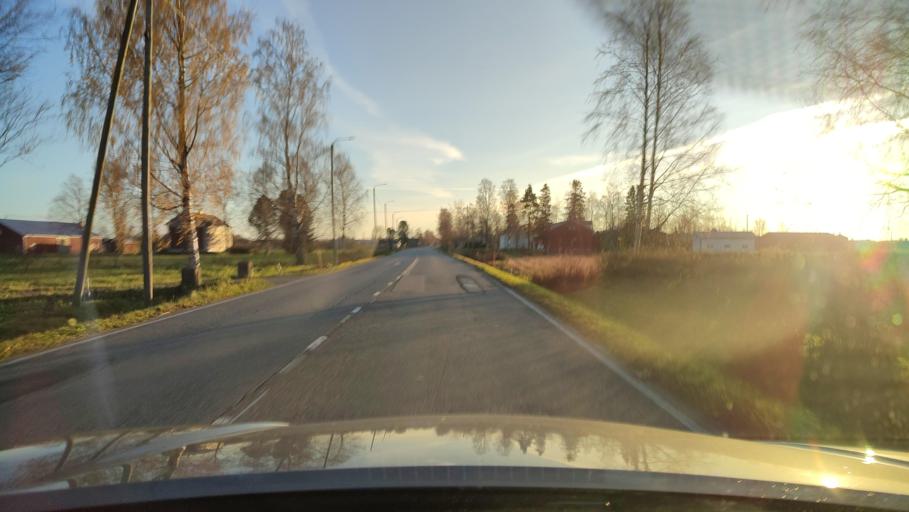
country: FI
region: Ostrobothnia
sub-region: Sydosterbotten
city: Naerpes
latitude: 62.6034
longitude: 21.4575
